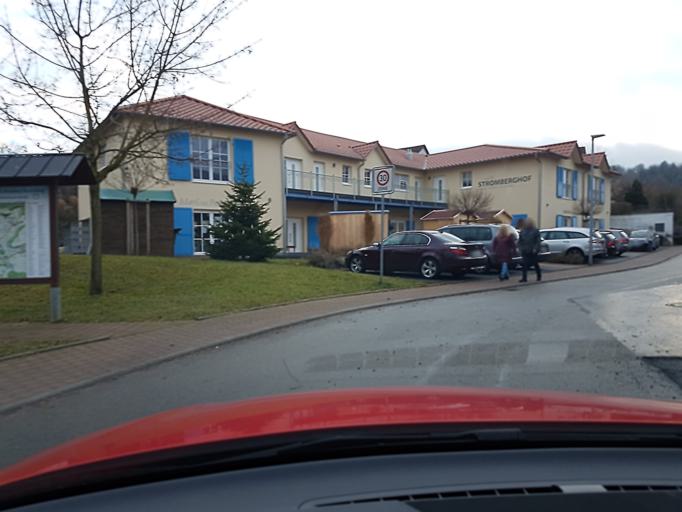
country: DE
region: Baden-Wuerttemberg
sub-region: Regierungsbezirk Stuttgart
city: Zaberfeld
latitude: 49.0581
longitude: 8.9247
